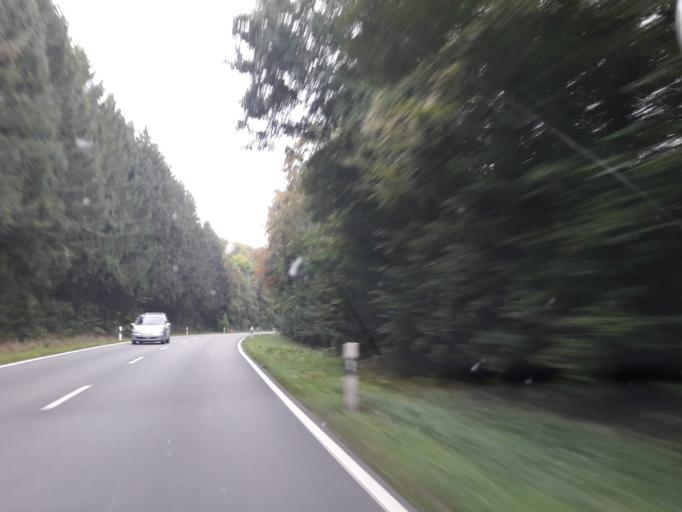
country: DE
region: Baden-Wuerttemberg
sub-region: Regierungsbezirk Stuttgart
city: Mockmuhl
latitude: 49.2871
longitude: 9.3606
